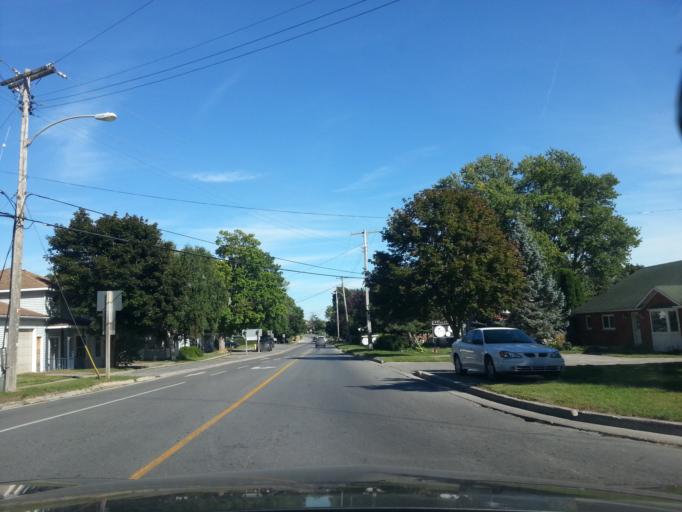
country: CA
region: Ontario
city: Prince Edward
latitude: 43.9862
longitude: -77.2383
